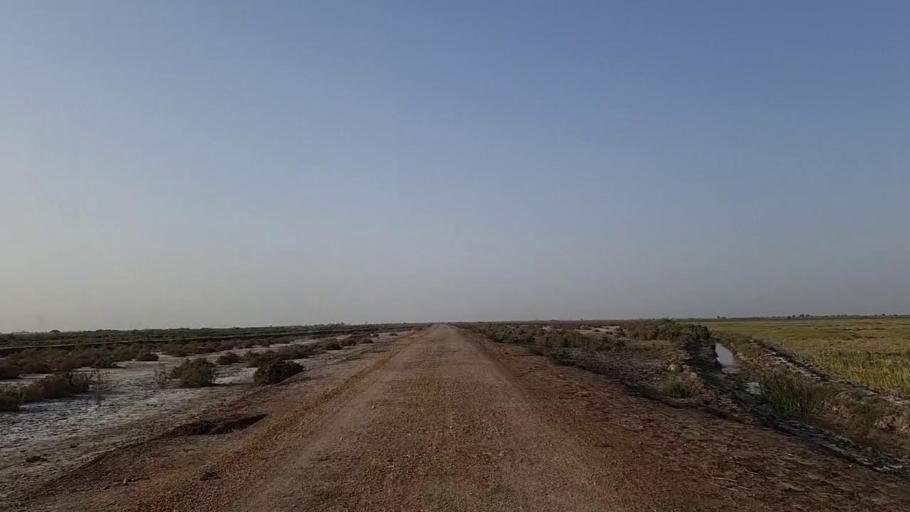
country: PK
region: Sindh
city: Jati
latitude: 24.3527
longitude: 68.1489
